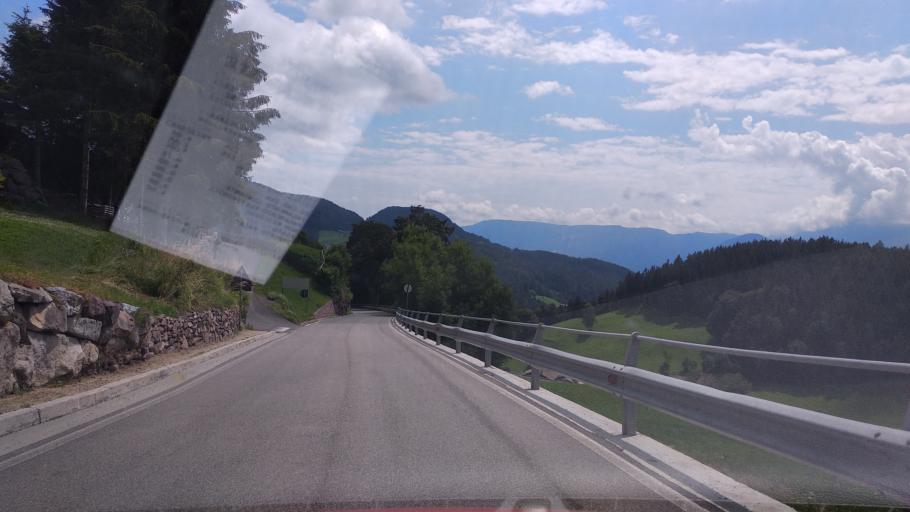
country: IT
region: Trentino-Alto Adige
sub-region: Bolzano
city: Avelengo
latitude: 46.6531
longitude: 11.2191
